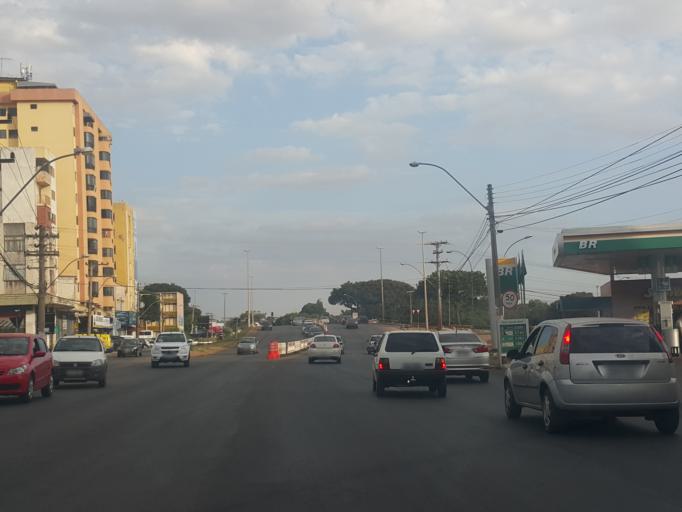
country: BR
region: Federal District
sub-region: Brasilia
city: Brasilia
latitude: -15.8330
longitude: -48.0609
